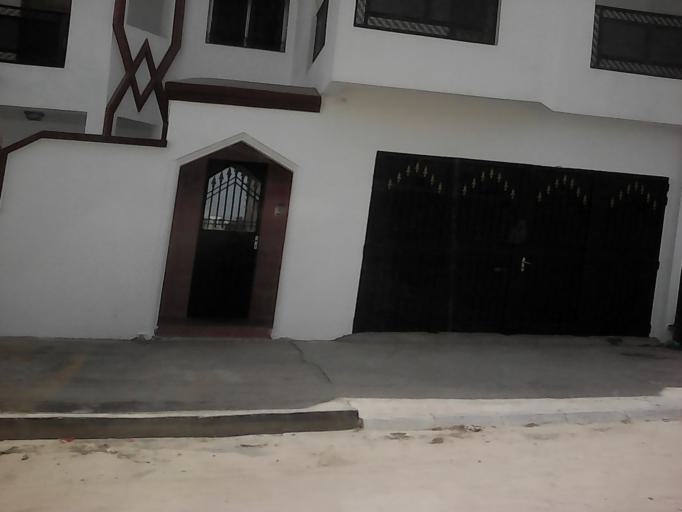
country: SN
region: Dakar
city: Grand Dakar
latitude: 14.7343
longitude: -17.4304
